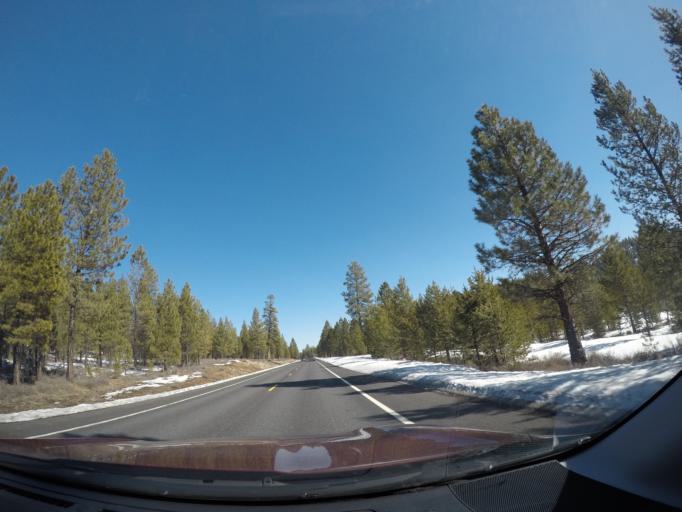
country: US
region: Oregon
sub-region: Deschutes County
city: Three Rivers
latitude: 43.8583
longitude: -121.5038
